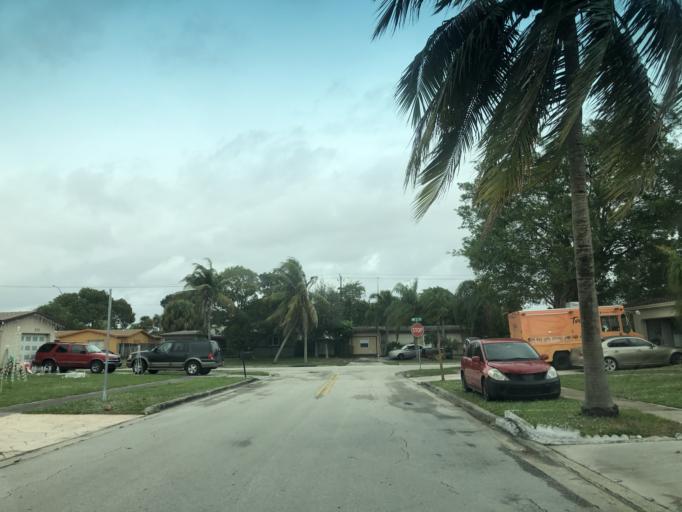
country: US
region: Florida
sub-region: Broward County
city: North Lauderdale
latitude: 26.2345
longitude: -80.2324
